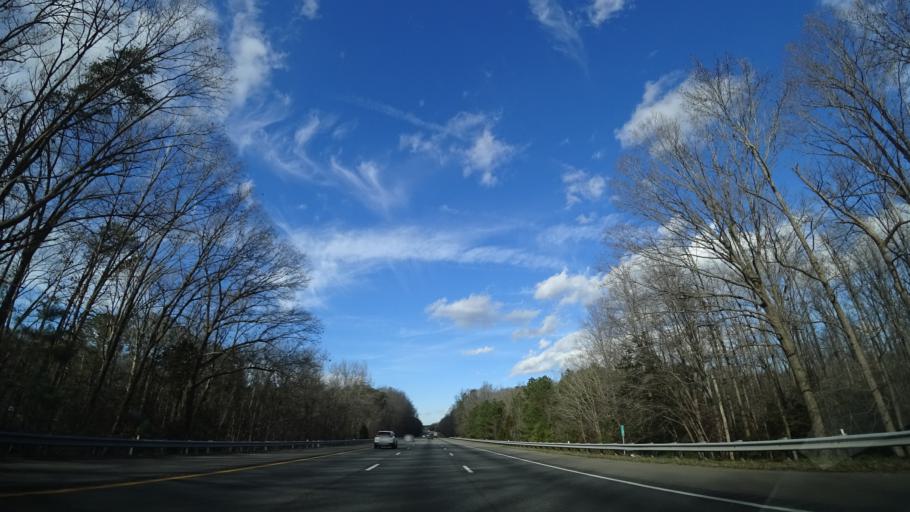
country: US
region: Virginia
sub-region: Caroline County
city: Bowling Green
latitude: 38.0547
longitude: -77.5018
